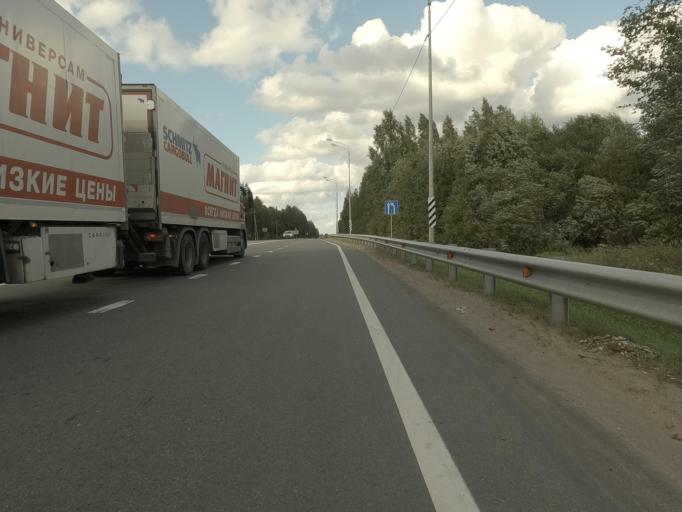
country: RU
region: Leningrad
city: Mga
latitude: 59.7379
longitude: 31.0738
